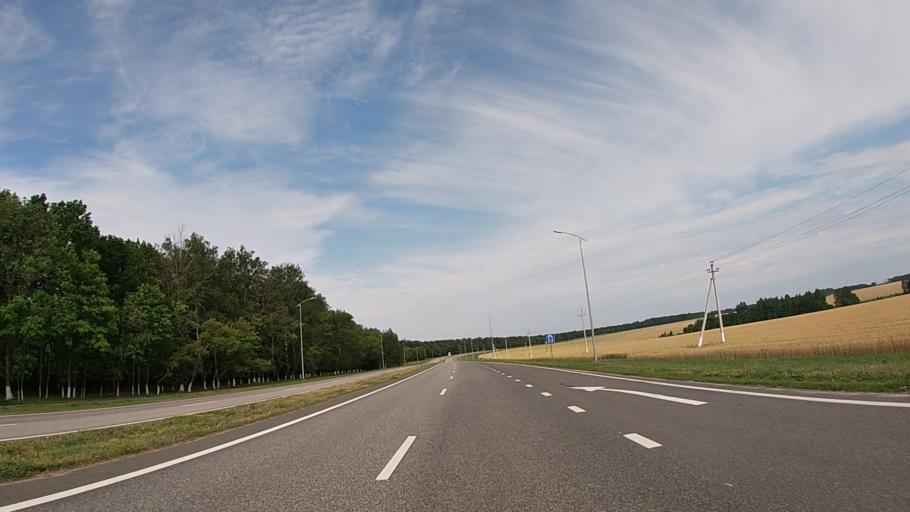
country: RU
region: Belgorod
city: Borisovka
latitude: 50.7510
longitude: 35.9799
